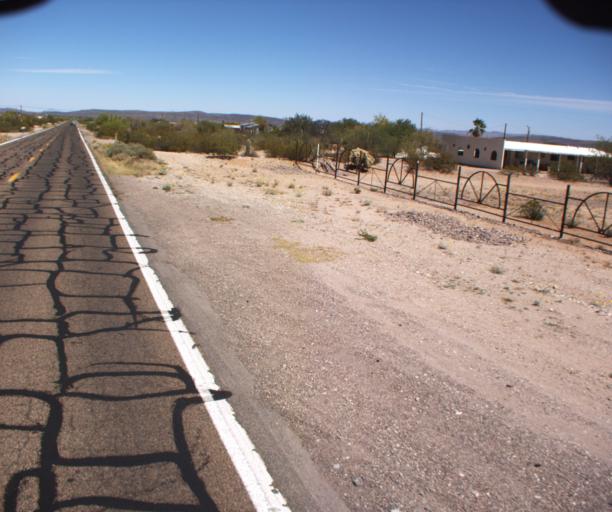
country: US
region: Arizona
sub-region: Pima County
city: Ajo
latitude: 32.4052
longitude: -112.8719
